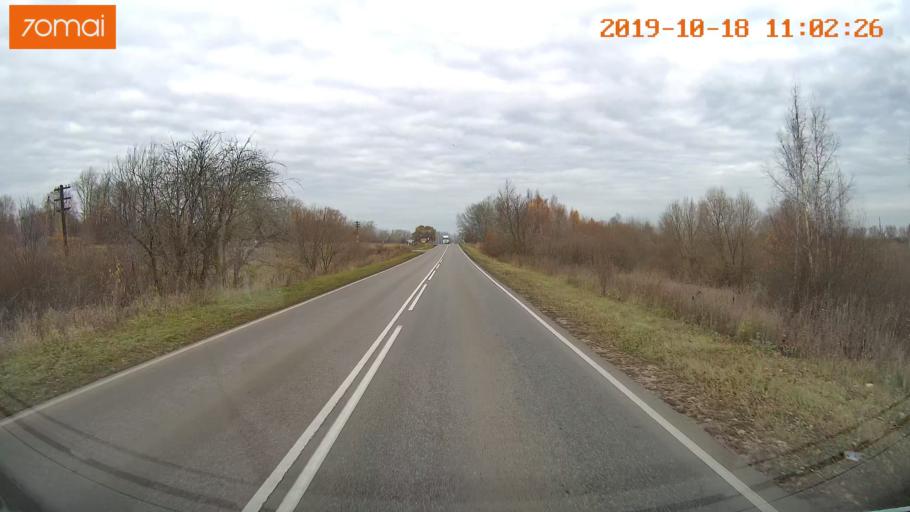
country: RU
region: Tula
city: Yepifan'
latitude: 53.8654
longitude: 38.5447
